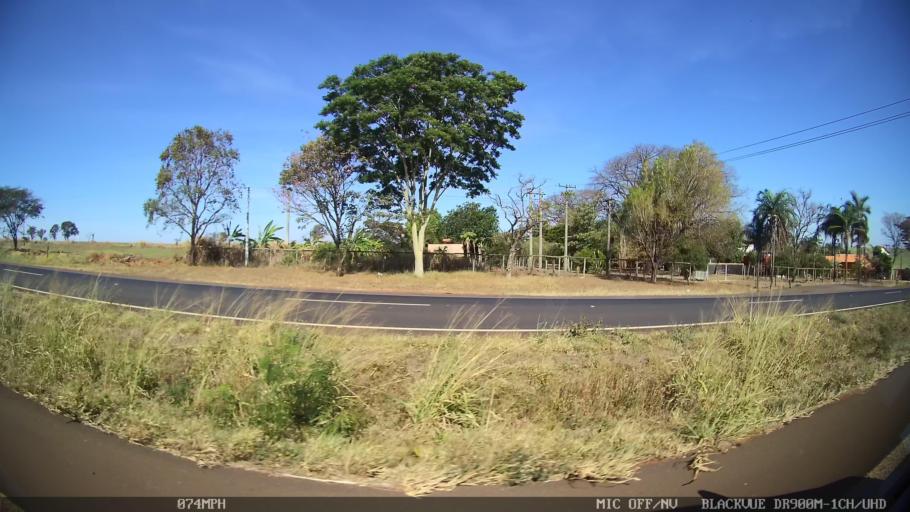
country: BR
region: Sao Paulo
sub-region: Barretos
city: Barretos
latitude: -20.5463
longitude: -48.6254
